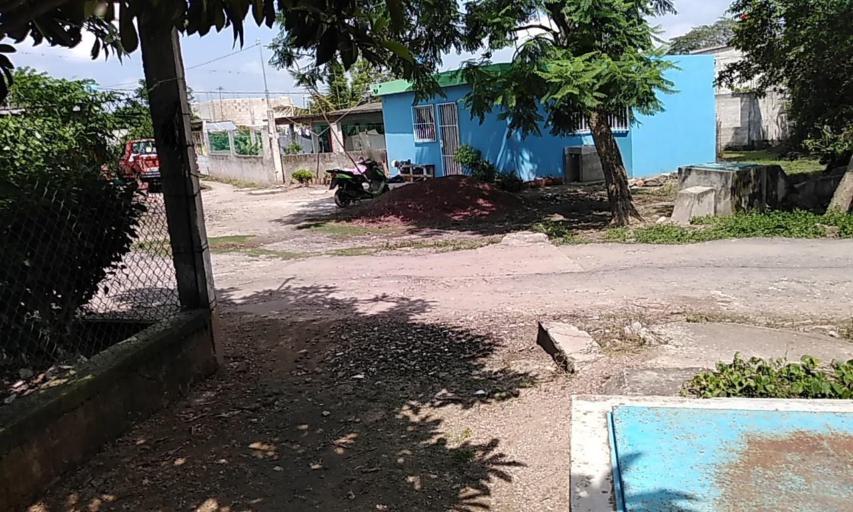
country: MX
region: Veracruz
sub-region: Emiliano Zapata
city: Dos Rios
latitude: 19.4438
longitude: -96.7829
